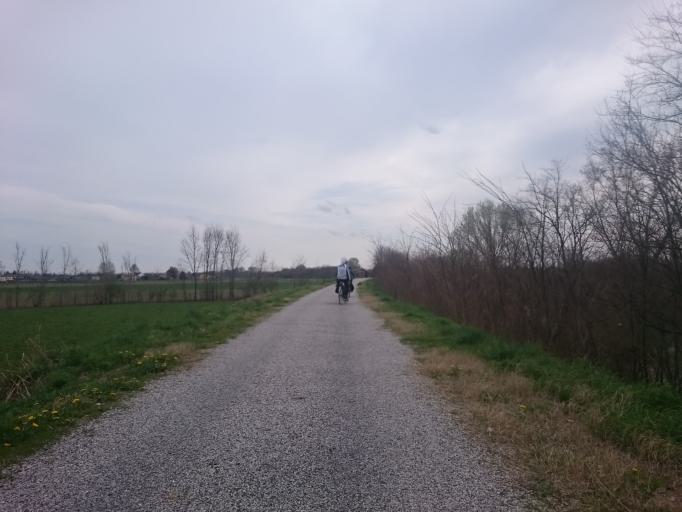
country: IT
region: Veneto
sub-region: Provincia di Padova
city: Saletto
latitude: 45.4686
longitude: 11.8637
